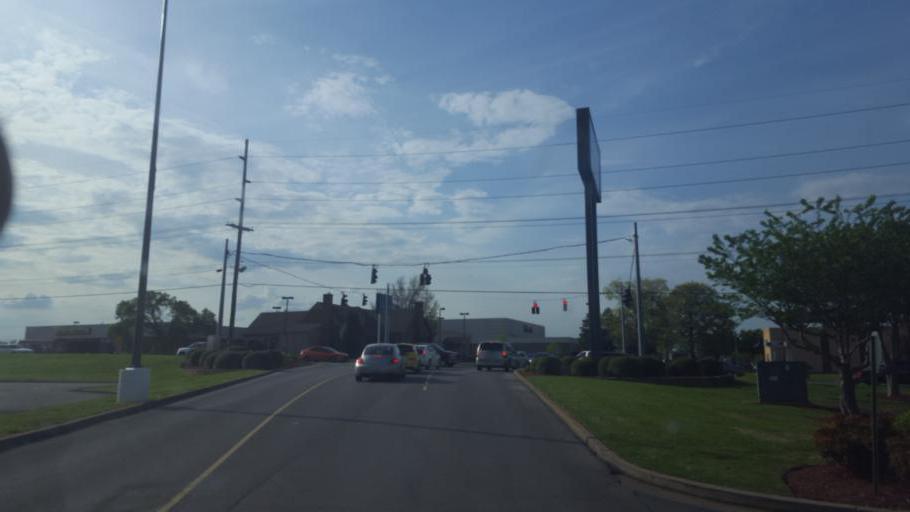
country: US
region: Kentucky
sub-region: Warren County
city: Bowling Green
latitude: 36.9449
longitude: -86.4246
